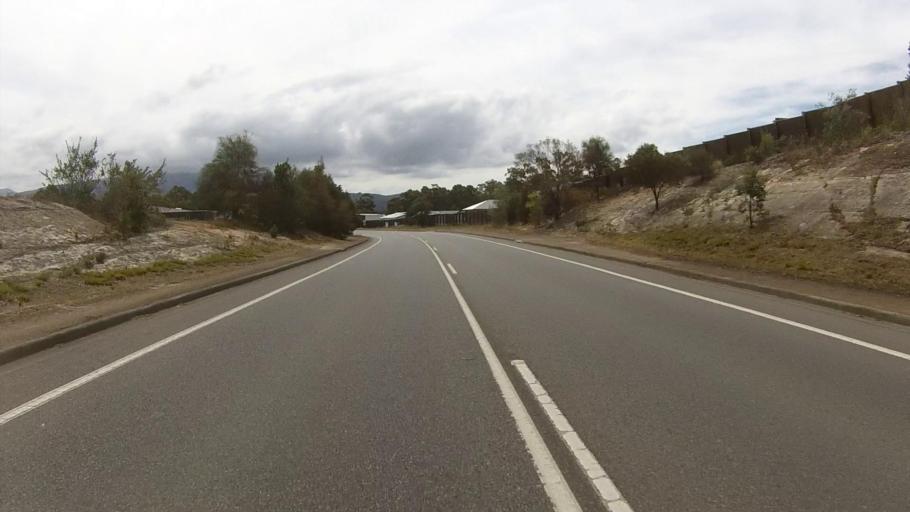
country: AU
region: Tasmania
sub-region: Kingborough
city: Kingston
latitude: -42.9907
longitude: 147.2942
